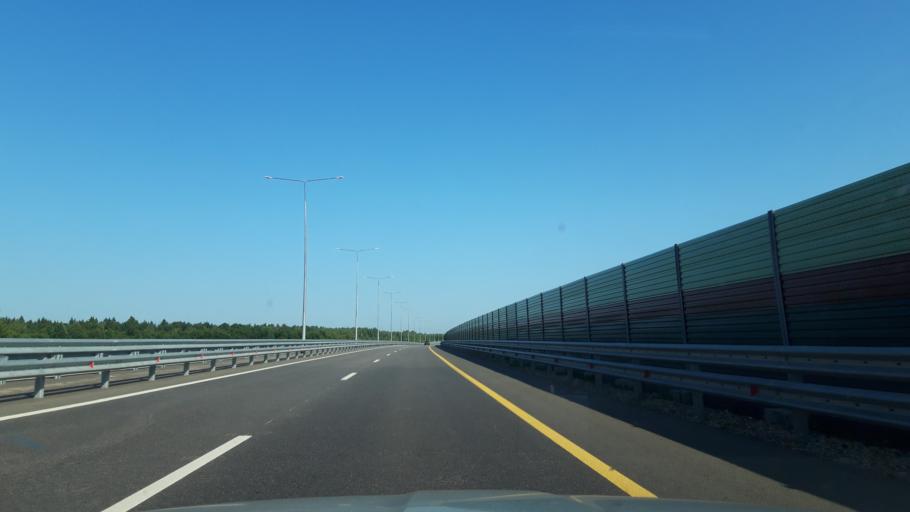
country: RU
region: Tverskaya
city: Zavidovo
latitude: 56.5121
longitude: 36.5098
